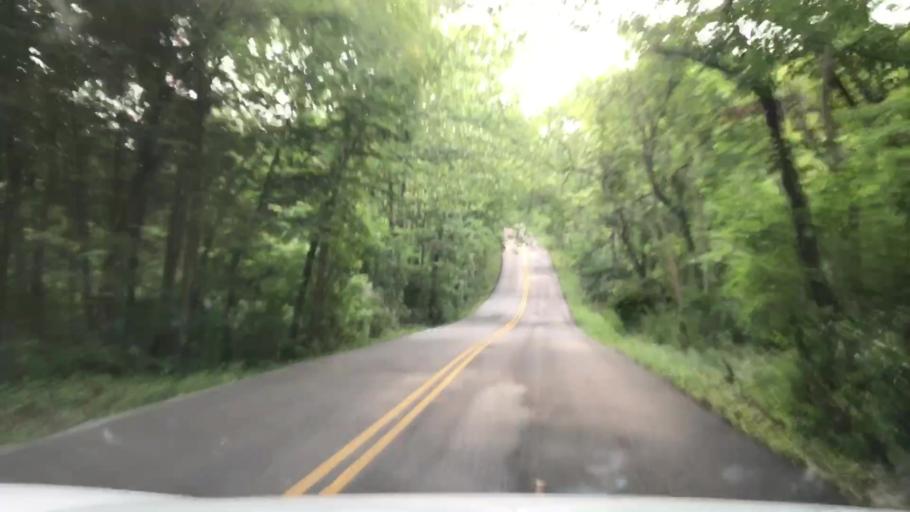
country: US
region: Missouri
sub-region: Saint Charles County
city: Cottleville
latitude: 38.7047
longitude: -90.6464
